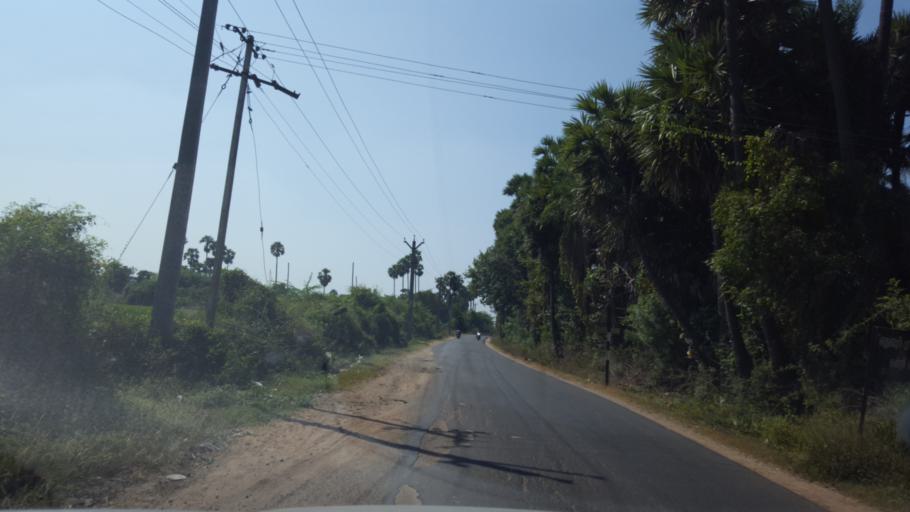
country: IN
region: Tamil Nadu
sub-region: Kancheepuram
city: Kanchipuram
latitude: 12.8377
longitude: 79.7289
